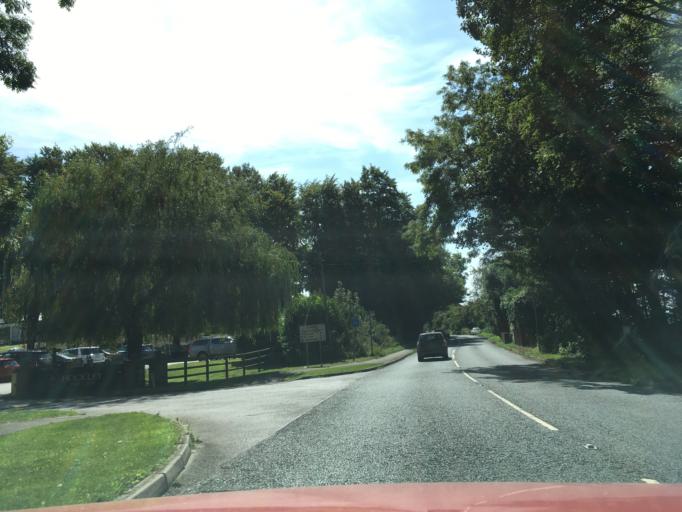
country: GB
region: England
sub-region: Hampshire
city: Compton
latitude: 51.0364
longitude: -1.3172
